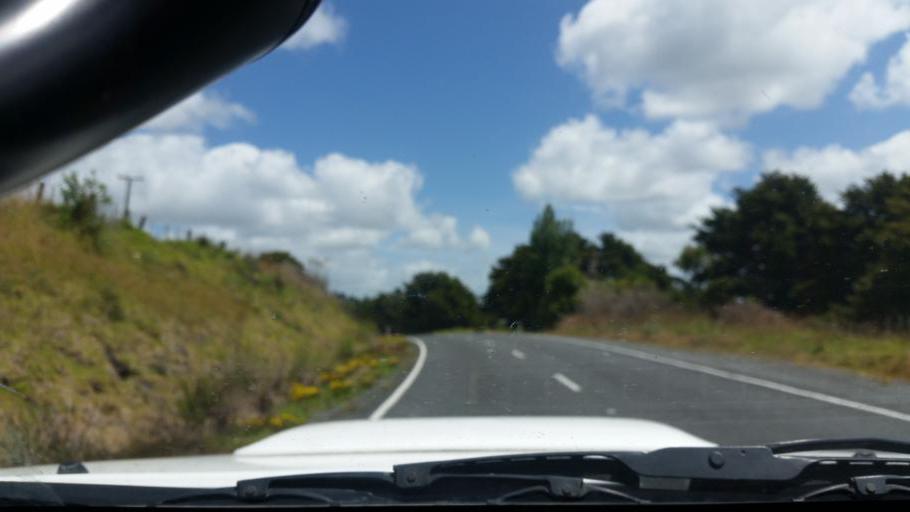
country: NZ
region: Northland
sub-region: Whangarei
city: Ruakaka
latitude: -36.0529
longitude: 174.2751
